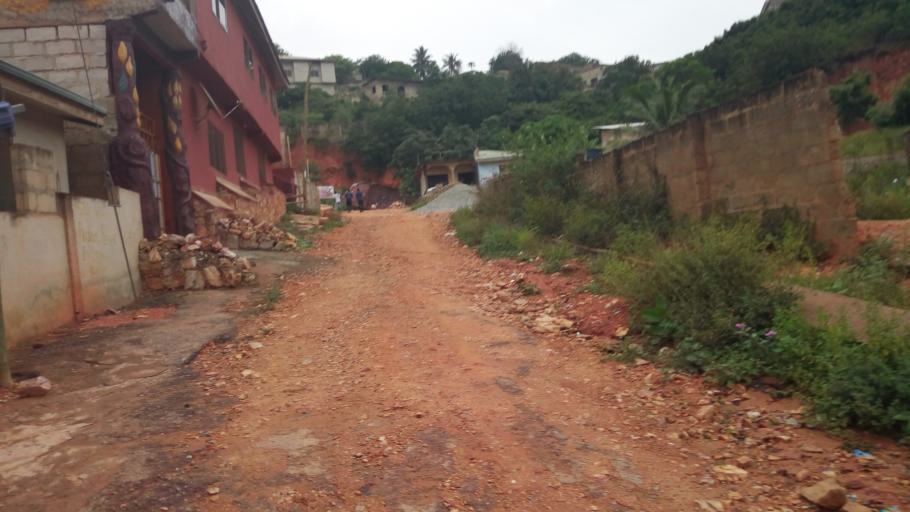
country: GH
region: Greater Accra
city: Gbawe
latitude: 5.5599
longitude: -0.3054
